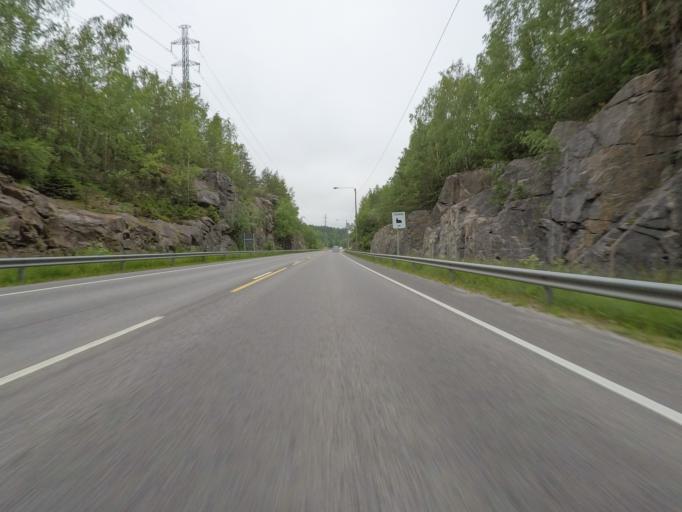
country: FI
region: Varsinais-Suomi
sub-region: Turku
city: Raisio
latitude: 60.4634
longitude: 22.1415
